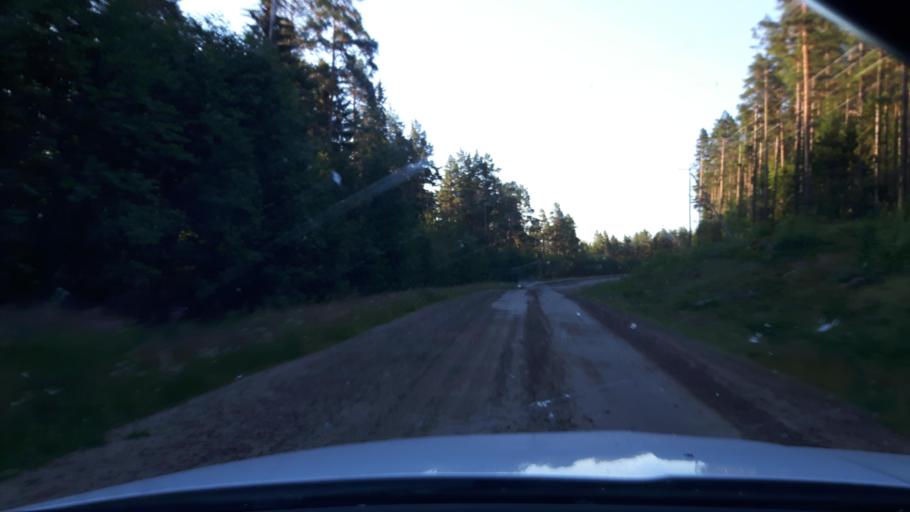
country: SE
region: Vaesternorrland
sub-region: Ange Kommun
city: Ange
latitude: 62.1670
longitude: 15.6540
